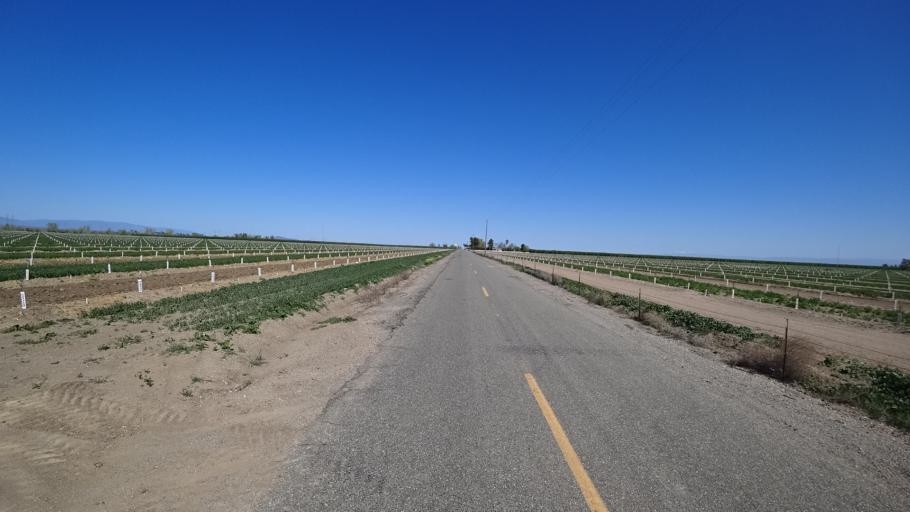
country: US
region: California
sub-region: Glenn County
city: Willows
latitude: 39.6348
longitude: -122.2535
